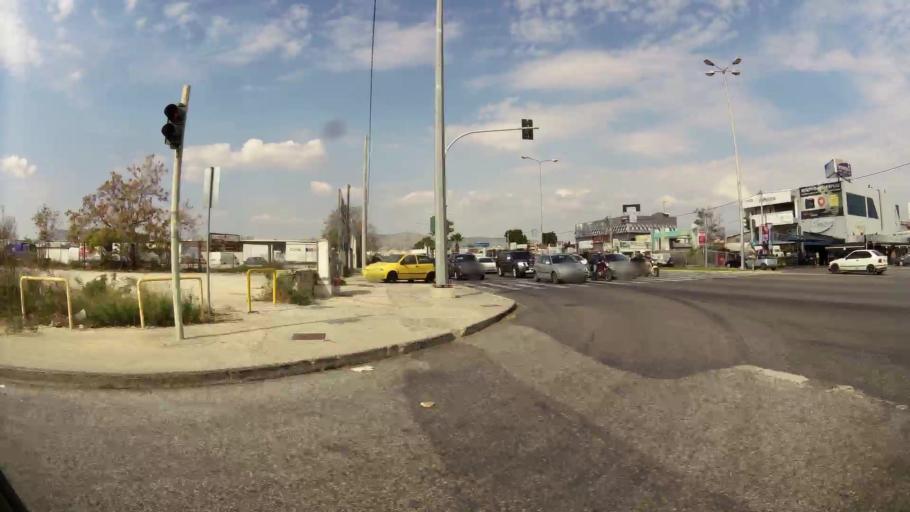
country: GR
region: Attica
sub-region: Nomarchia Athinas
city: Aigaleo
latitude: 37.9933
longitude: 23.6982
